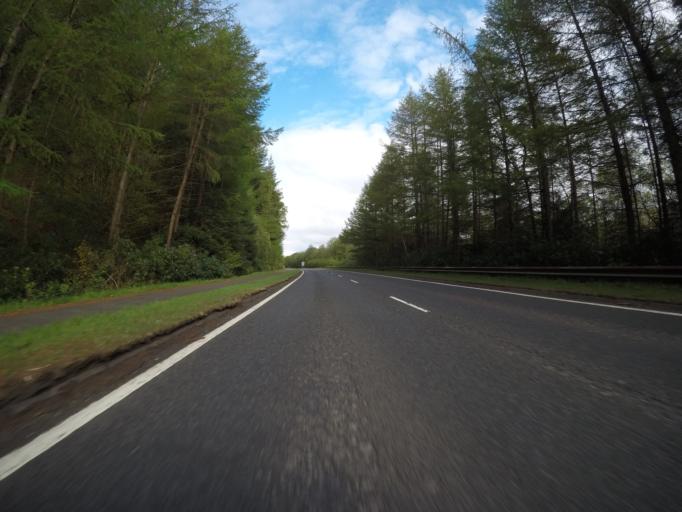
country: GB
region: Scotland
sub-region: Highland
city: Fort William
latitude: 56.6804
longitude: -5.1601
